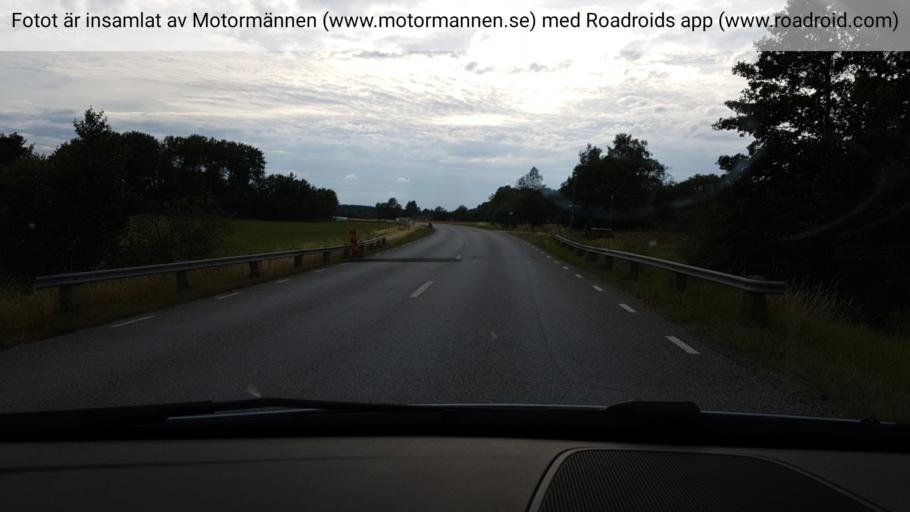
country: SE
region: Stockholm
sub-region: Norrtalje Kommun
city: Skanninge
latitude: 59.8986
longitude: 18.3792
